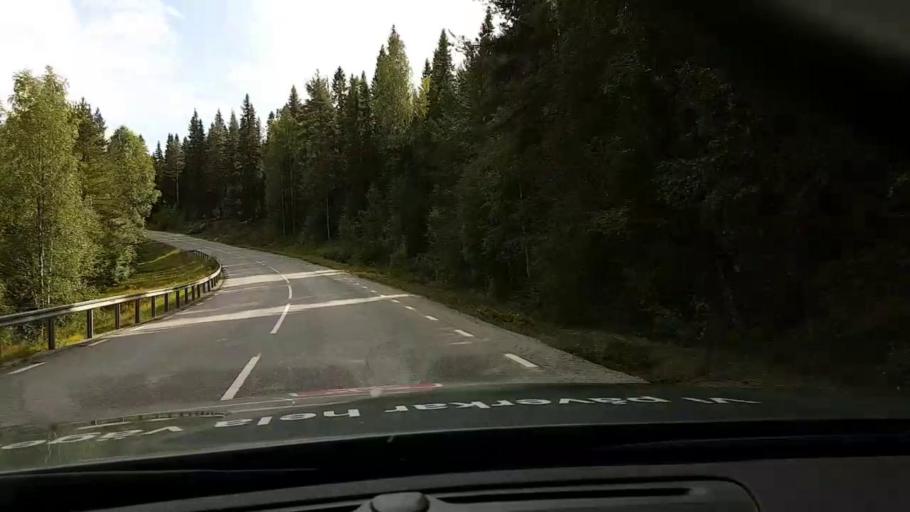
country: SE
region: Vaesternorrland
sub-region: OErnskoeldsviks Kommun
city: Bredbyn
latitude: 63.6435
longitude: 17.8966
